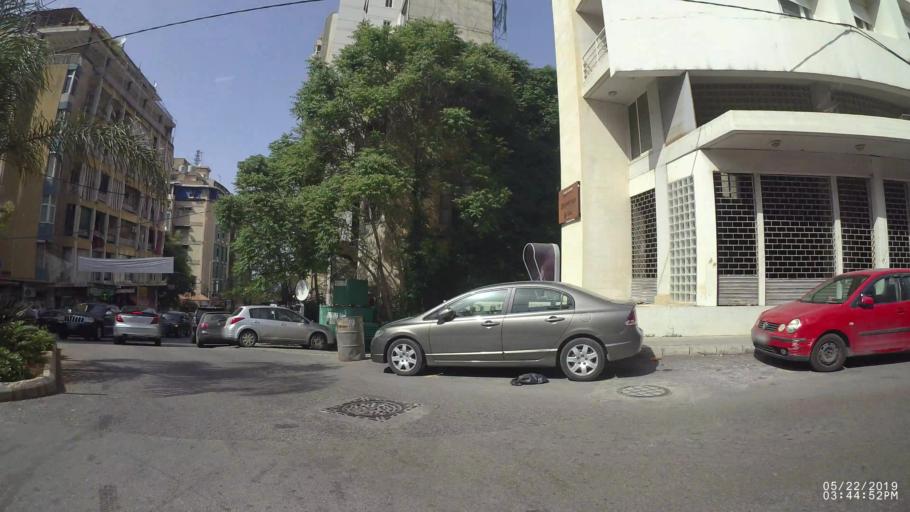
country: LB
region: Beyrouth
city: Ra's Bayrut
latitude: 33.8996
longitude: 35.4894
